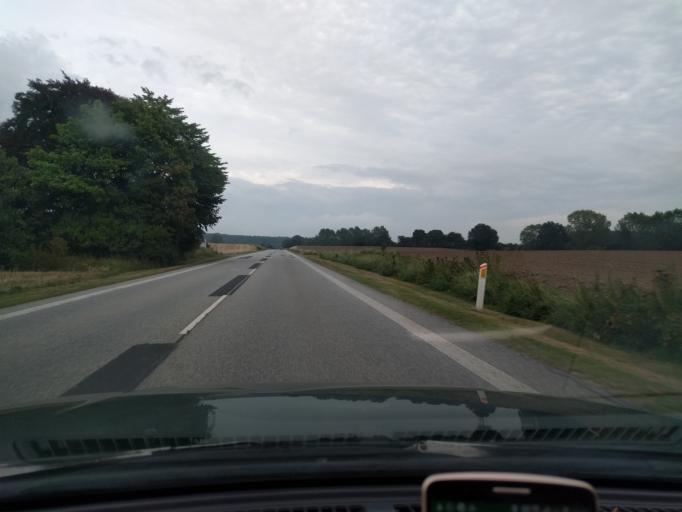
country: DK
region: Zealand
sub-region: Naestved Kommune
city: Naestved
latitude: 55.2069
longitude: 11.6506
